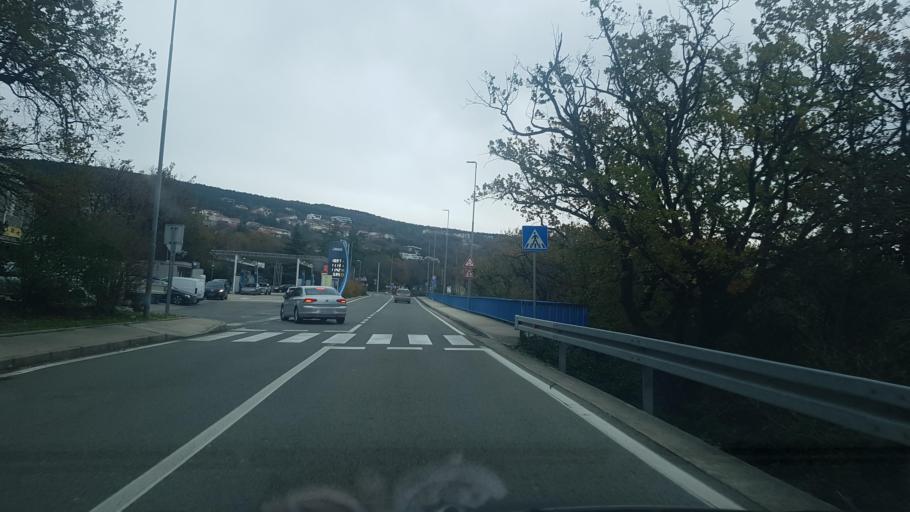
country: HR
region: Primorsko-Goranska
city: Cernik
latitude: 45.3097
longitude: 14.4867
